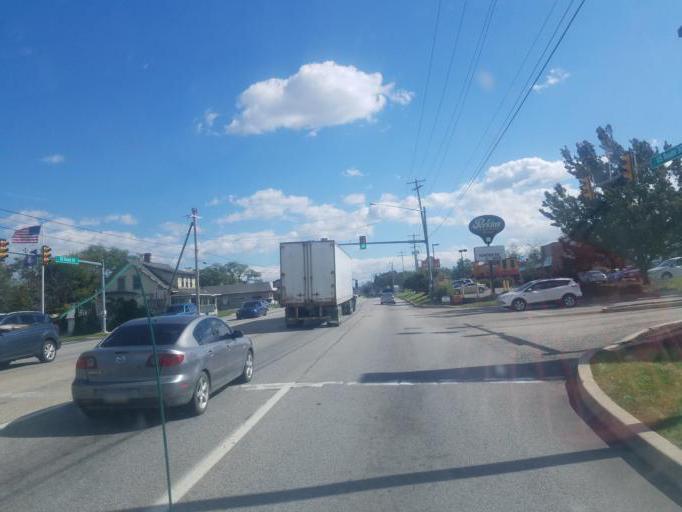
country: US
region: Pennsylvania
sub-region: Franklin County
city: Guilford
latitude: 39.9275
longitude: -77.6297
